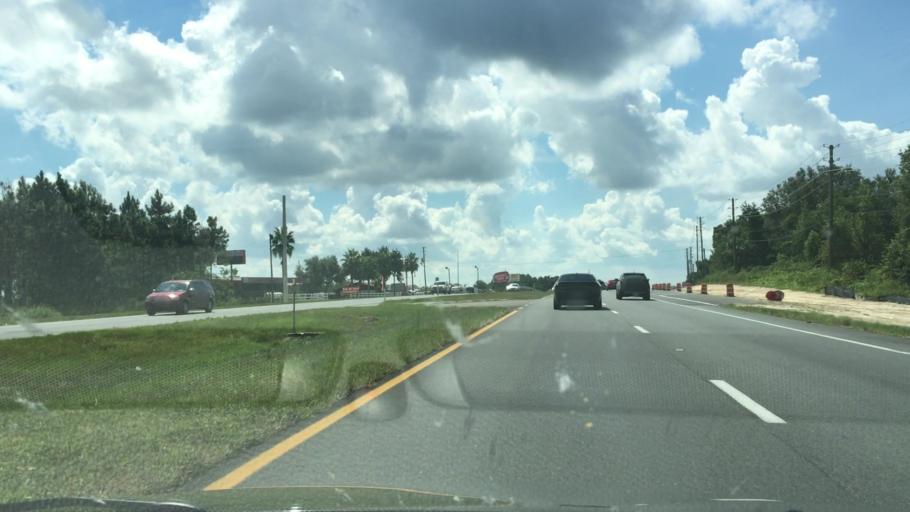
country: US
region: Florida
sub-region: Lake County
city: Minneola
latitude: 28.6064
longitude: -81.7568
